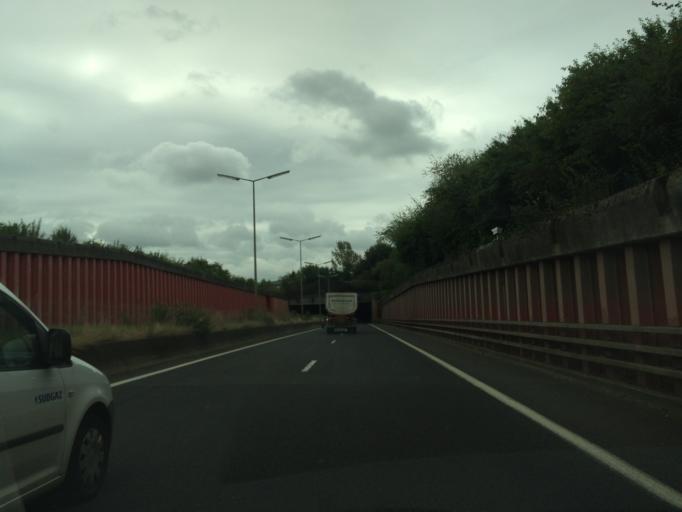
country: LU
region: Luxembourg
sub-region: Canton d'Esch-sur-Alzette
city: Mondercange
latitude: 49.5264
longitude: 5.9667
